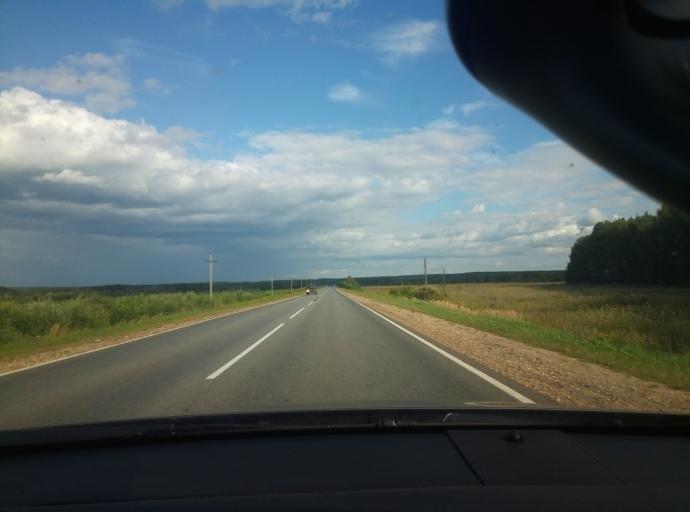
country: RU
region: Kaluga
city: Nikola-Lenivets
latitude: 54.5695
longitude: 35.4600
